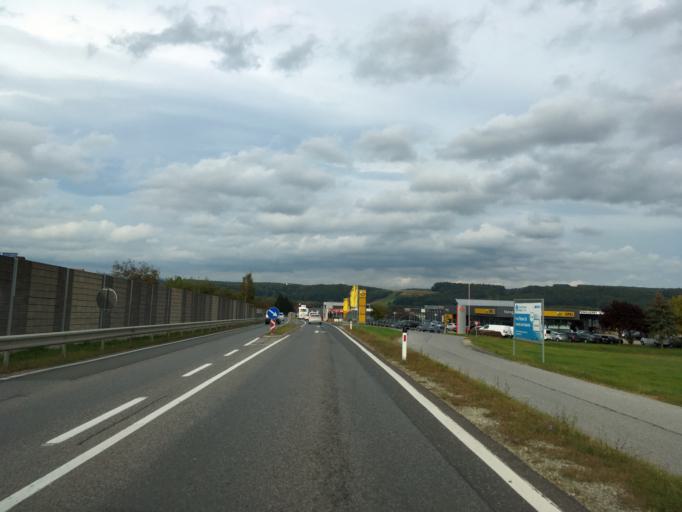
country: AT
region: Styria
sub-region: Politischer Bezirk Hartberg-Fuerstenfeld
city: Grafendorf bei Hartberg
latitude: 47.3242
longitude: 15.9892
